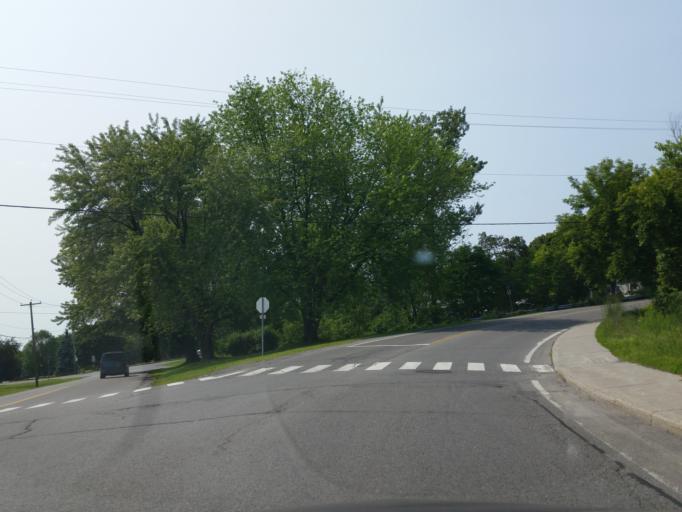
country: CA
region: Ontario
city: Bells Corners
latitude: 45.3887
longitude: -75.8397
